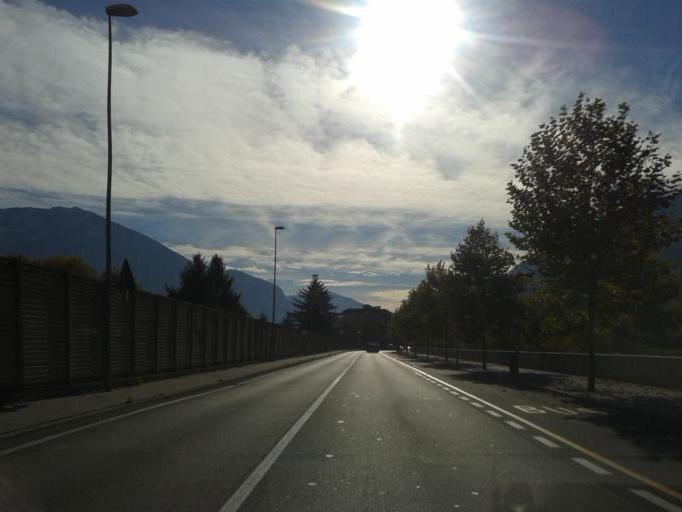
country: IT
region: Trentino-Alto Adige
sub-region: Provincia di Trento
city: Ravina
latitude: 46.0548
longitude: 11.1122
